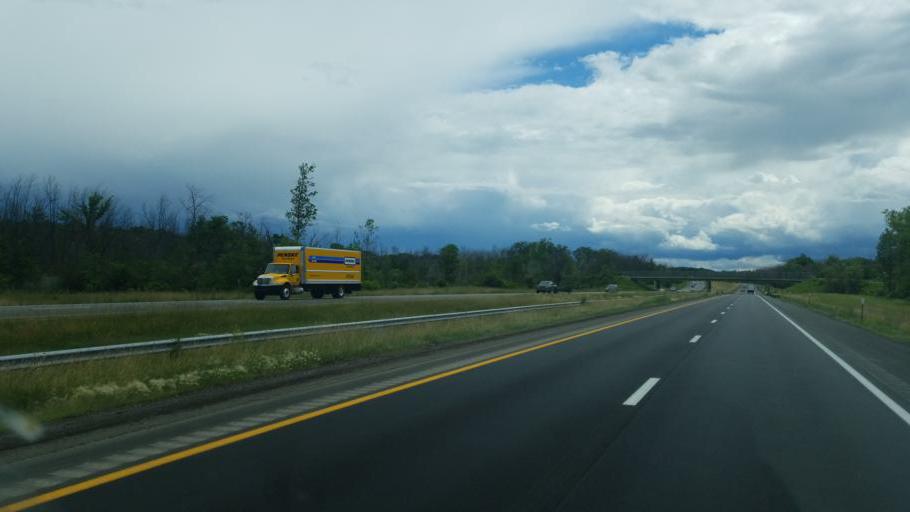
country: US
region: New York
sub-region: Livingston County
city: Caledonia
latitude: 43.0296
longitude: -77.8473
